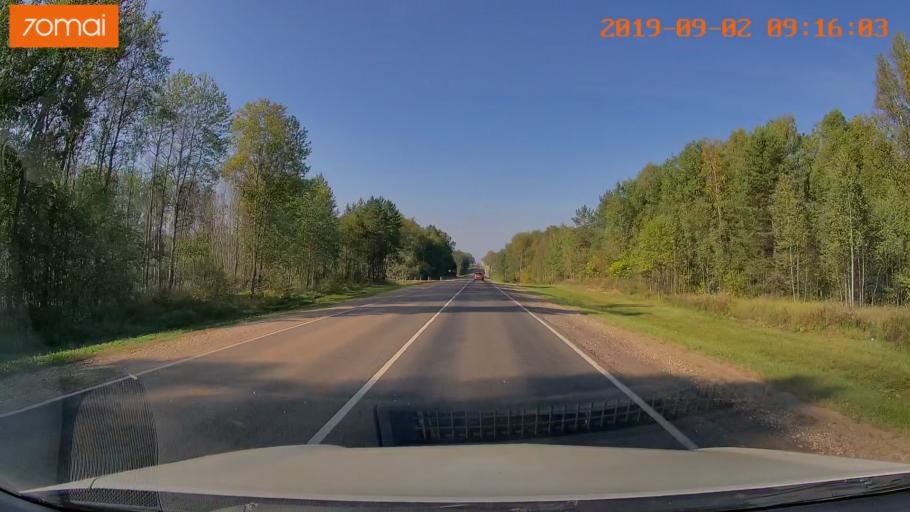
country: RU
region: Kaluga
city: Nikola-Lenivets
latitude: 54.8350
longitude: 35.4825
